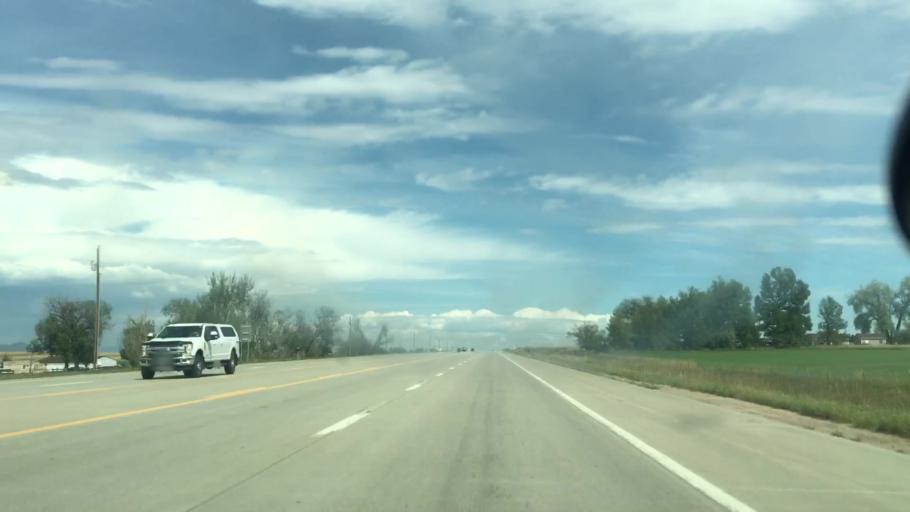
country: US
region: Colorado
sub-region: Boulder County
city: Longmont
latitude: 40.2127
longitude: -105.1023
